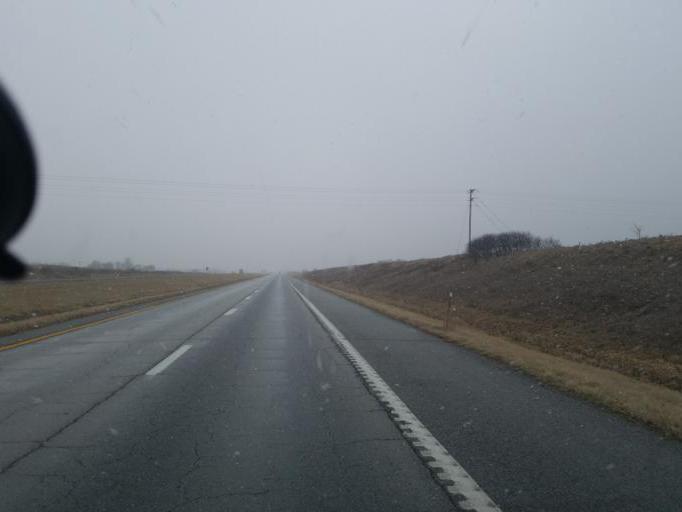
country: US
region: Missouri
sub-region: Macon County
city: La Plata
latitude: 39.9559
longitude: -92.4768
